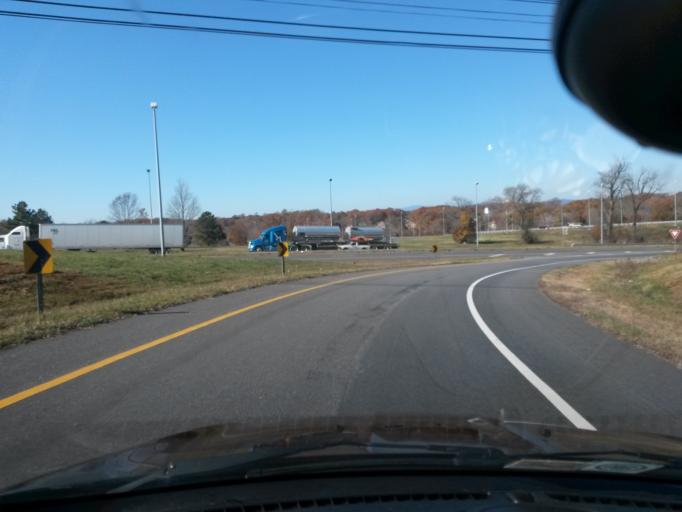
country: US
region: Virginia
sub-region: City of Lynchburg
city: West Lynchburg
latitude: 37.3386
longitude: -79.1904
